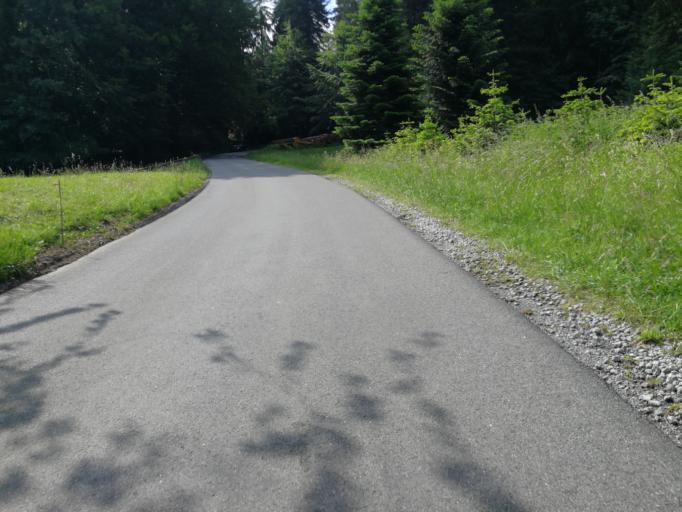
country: CH
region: Schwyz
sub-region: Bezirk Hoefe
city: Freienbach
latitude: 47.1828
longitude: 8.7753
